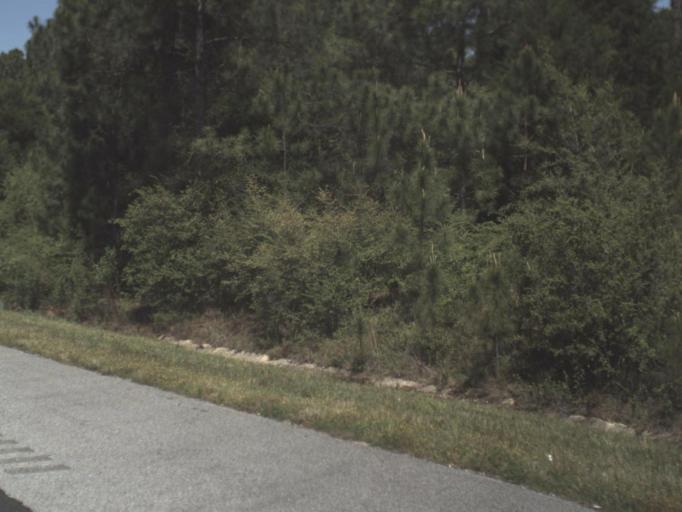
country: US
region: Florida
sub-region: Escambia County
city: Cantonment
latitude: 30.5700
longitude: -87.4001
